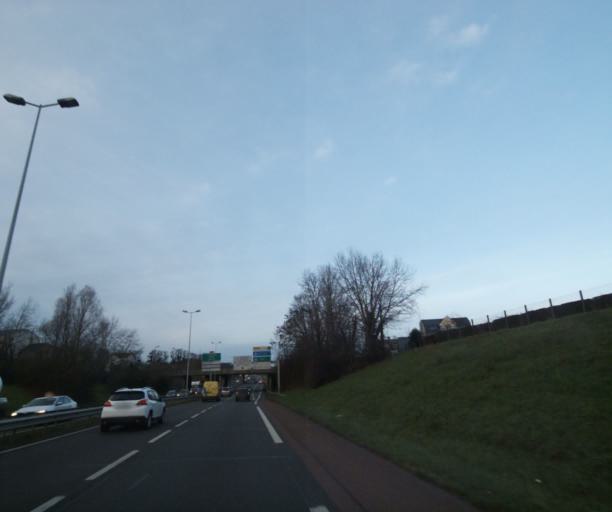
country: FR
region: Pays de la Loire
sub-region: Departement de la Sarthe
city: La Chapelle-Saint-Aubin
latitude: 48.0125
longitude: 0.1710
